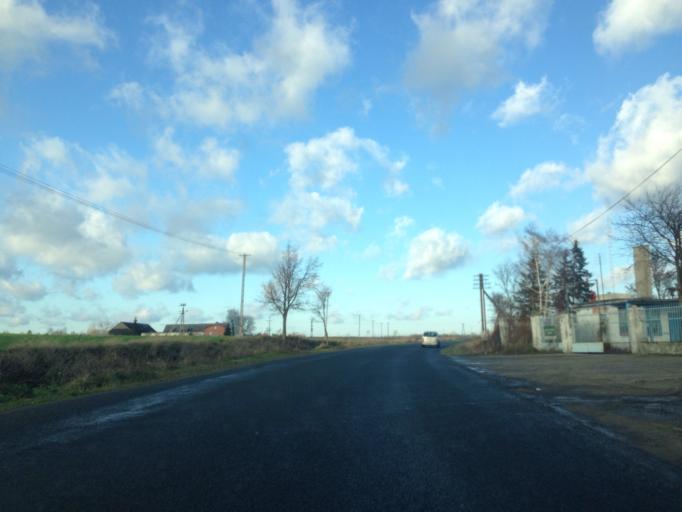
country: PL
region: Kujawsko-Pomorskie
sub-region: Powiat grudziadzki
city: Lasin
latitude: 53.5292
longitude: 19.0728
